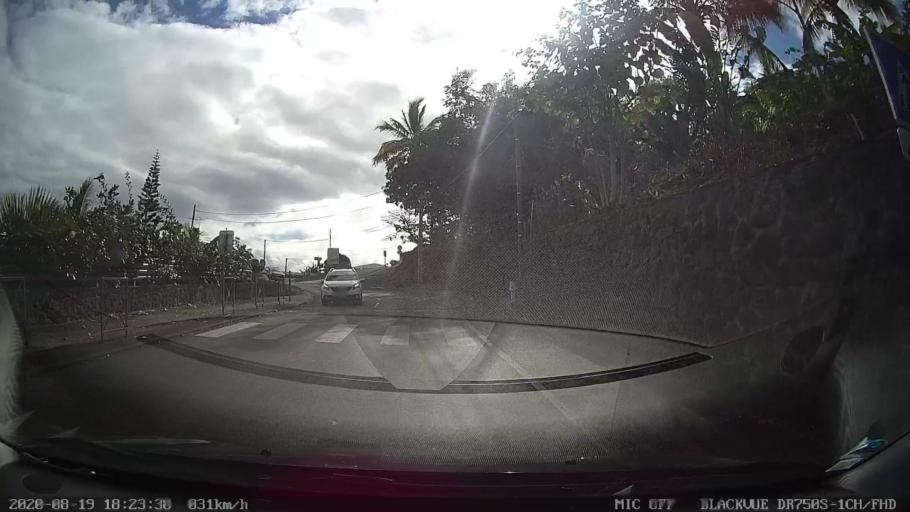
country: RE
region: Reunion
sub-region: Reunion
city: La Possession
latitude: -20.9520
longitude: 55.3427
